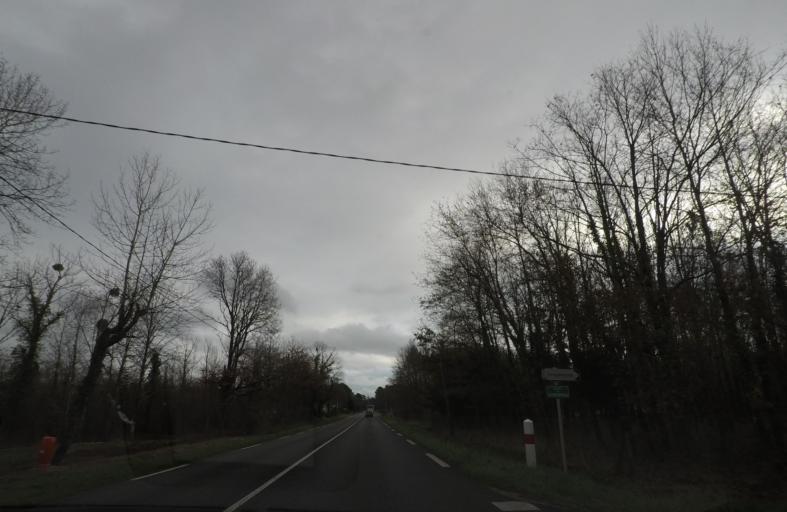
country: FR
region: Centre
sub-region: Departement du Loir-et-Cher
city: Mur-de-Sologne
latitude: 47.4064
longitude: 1.6192
